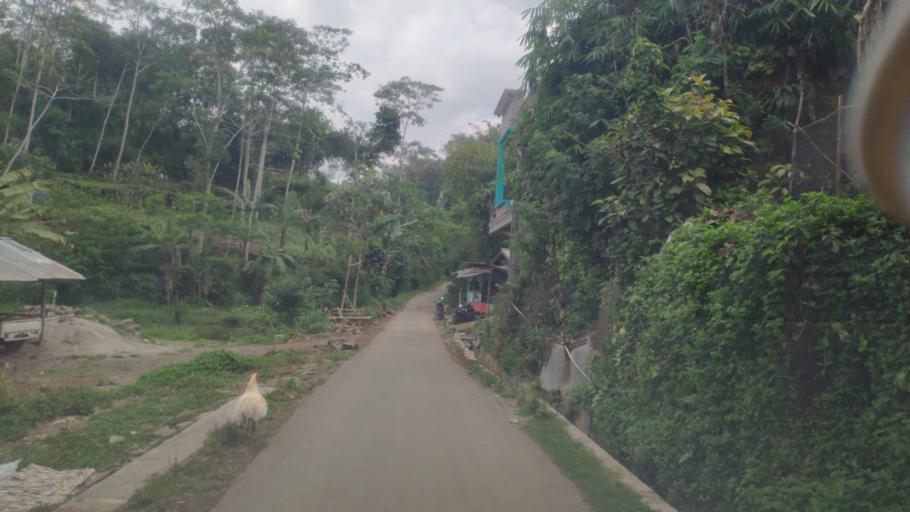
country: ID
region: Central Java
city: Wonosobo
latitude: -7.2691
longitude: 109.7519
